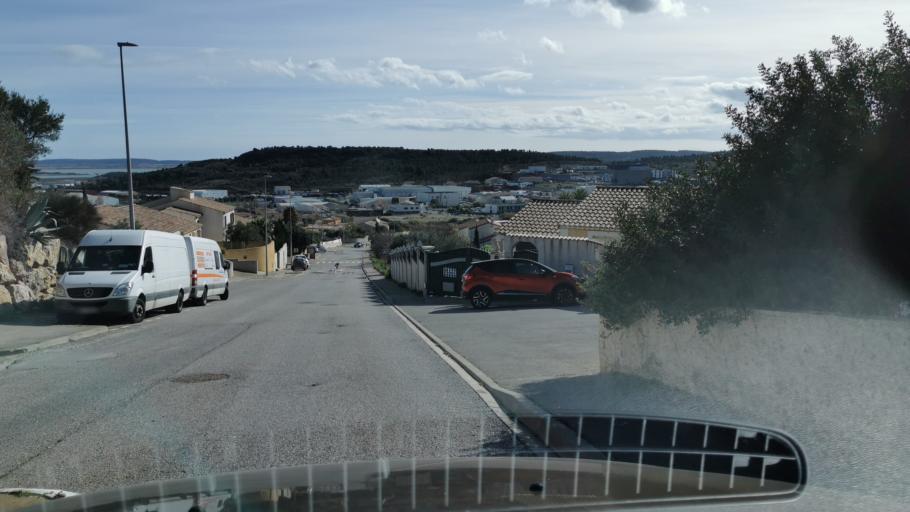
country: FR
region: Languedoc-Roussillon
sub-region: Departement de l'Aude
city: Narbonne
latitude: 43.1636
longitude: 2.9665
